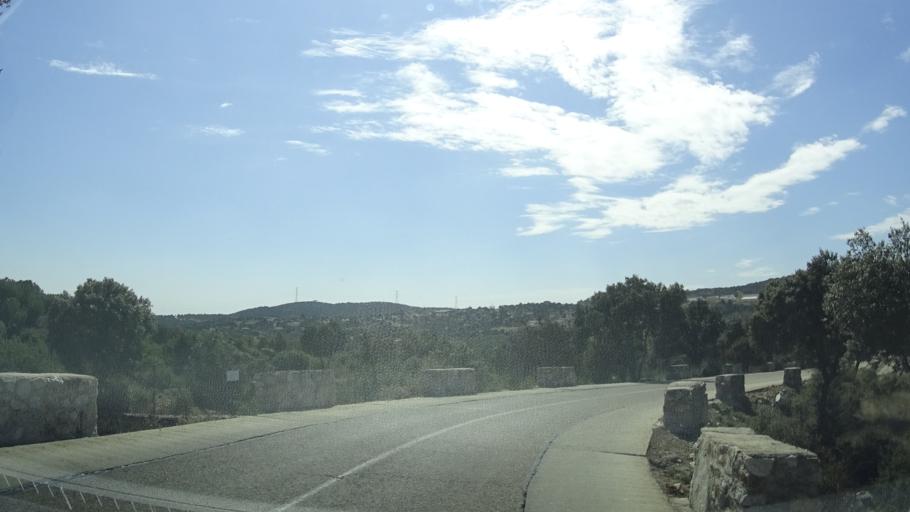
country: ES
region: Madrid
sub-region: Provincia de Madrid
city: Hoyo de Manzanares
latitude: 40.6305
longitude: -3.8707
